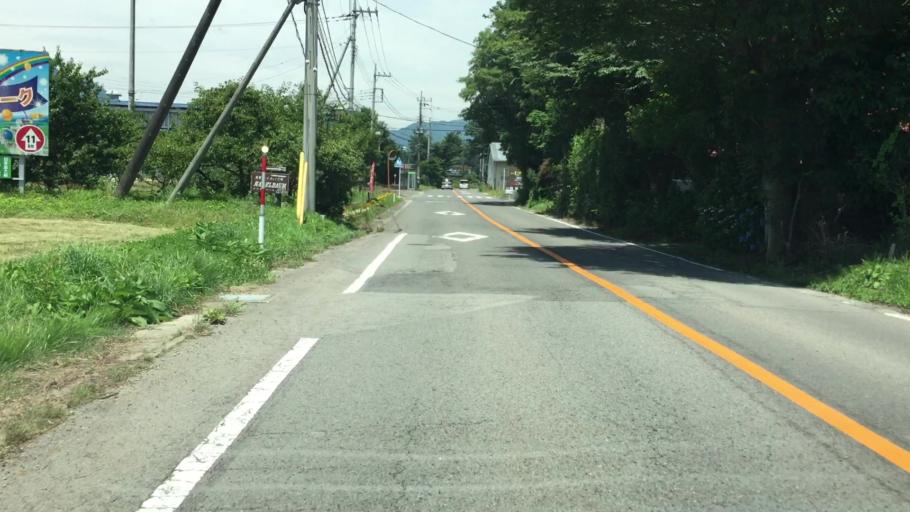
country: JP
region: Tochigi
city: Kuroiso
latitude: 37.0309
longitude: 139.9444
